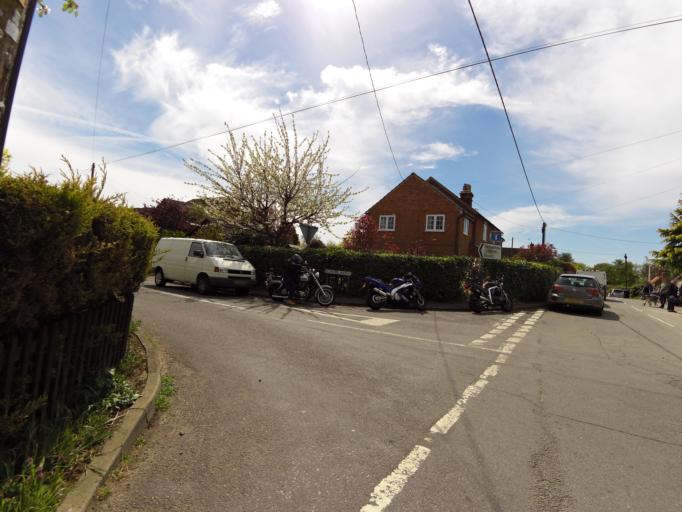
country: GB
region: England
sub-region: Essex
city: Mistley
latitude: 52.0019
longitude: 1.1118
